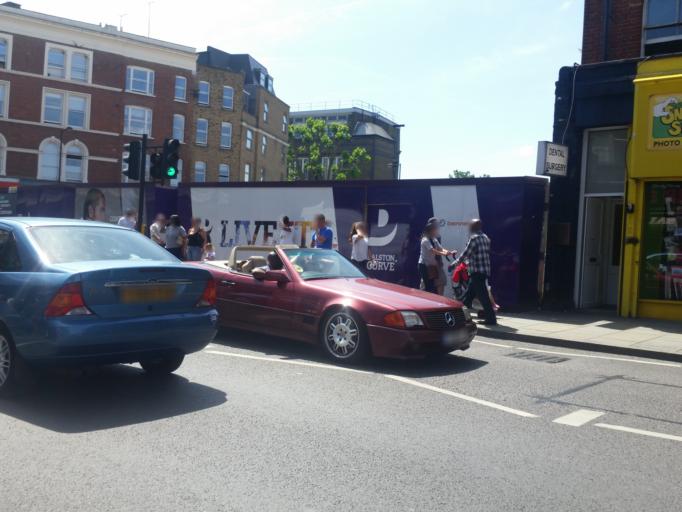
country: GB
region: England
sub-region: Greater London
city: Bethnal Green
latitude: 51.5474
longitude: -0.0756
